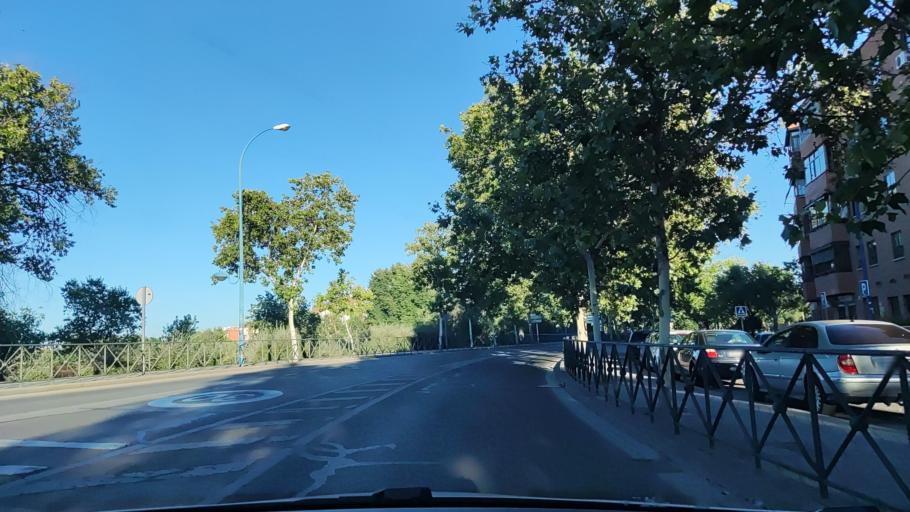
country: ES
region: Madrid
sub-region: Provincia de Madrid
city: Leganes
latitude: 40.3364
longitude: -3.7643
